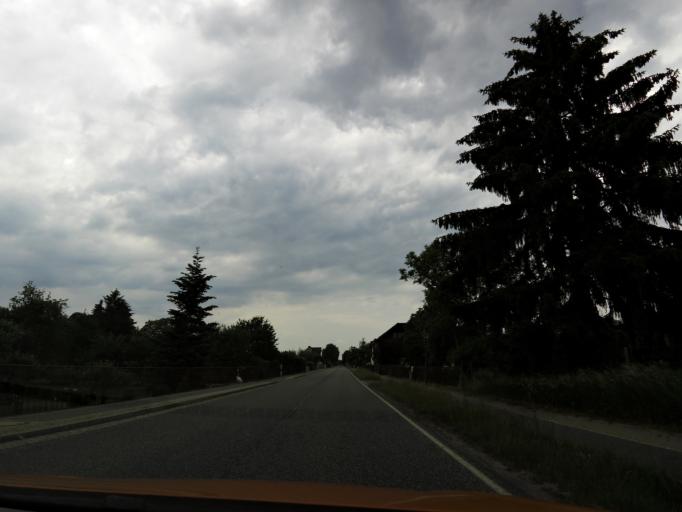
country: DE
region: Brandenburg
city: Baruth
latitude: 52.0533
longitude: 13.5056
